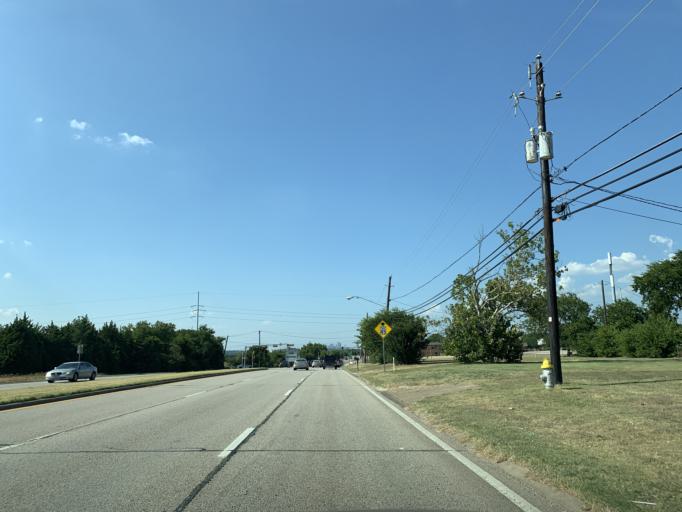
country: US
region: Texas
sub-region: Dallas County
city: Hutchins
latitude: 32.6611
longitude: -96.7836
